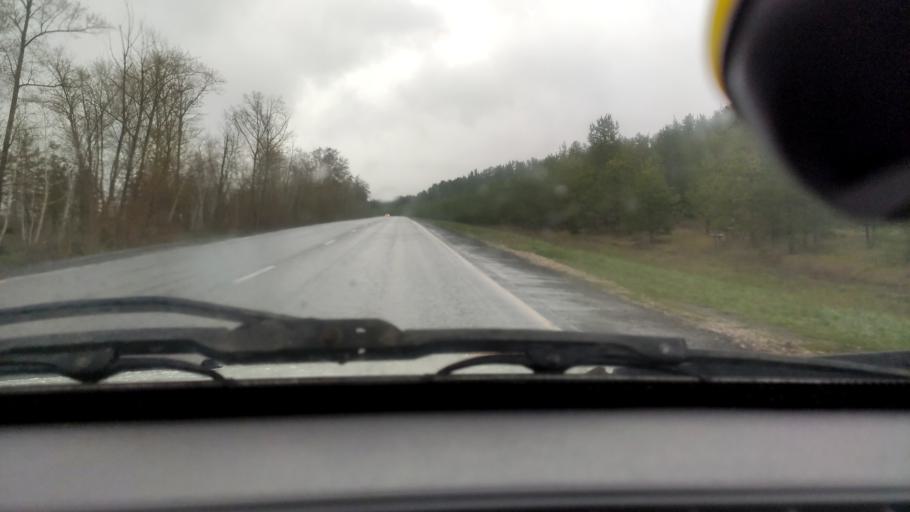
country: RU
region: Samara
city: Povolzhskiy
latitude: 53.6232
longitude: 49.6461
